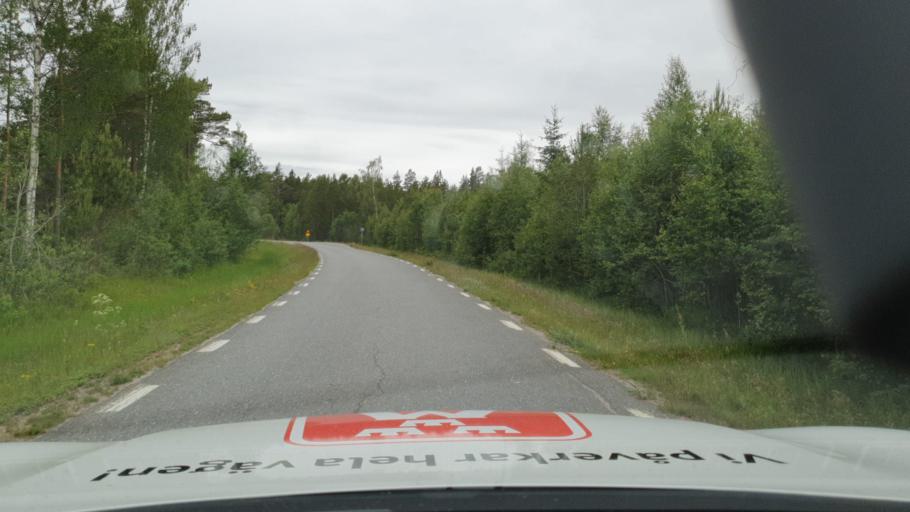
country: SE
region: Vaesterbotten
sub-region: Nordmalings Kommun
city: Nordmaling
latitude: 63.4326
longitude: 19.4866
